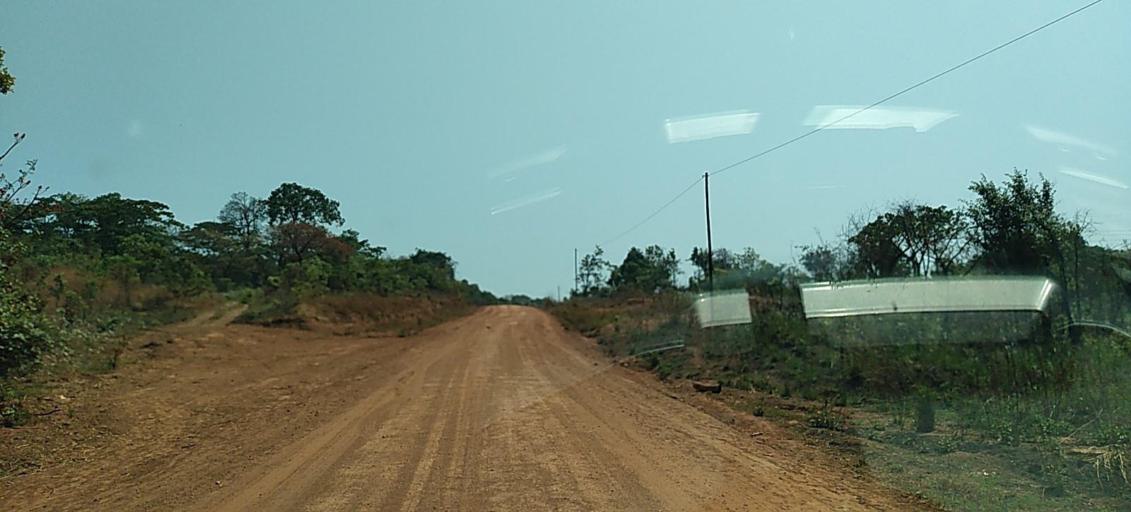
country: ZM
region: North-Western
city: Kansanshi
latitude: -11.9949
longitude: 26.6160
